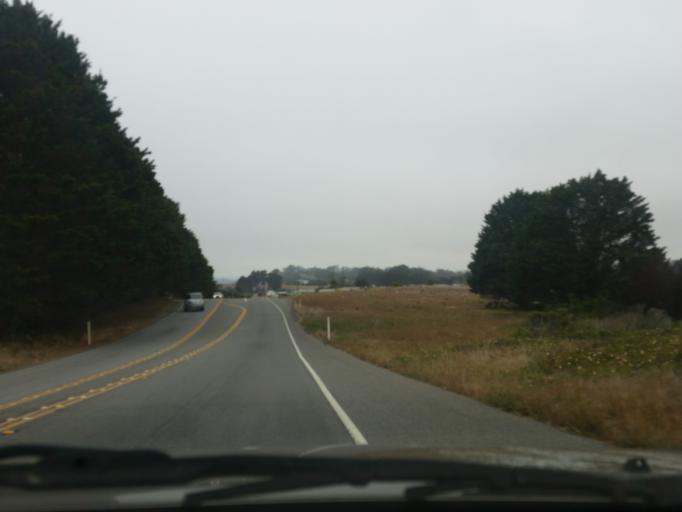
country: US
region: California
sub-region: San Luis Obispo County
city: Callender
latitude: 35.0730
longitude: -120.5906
